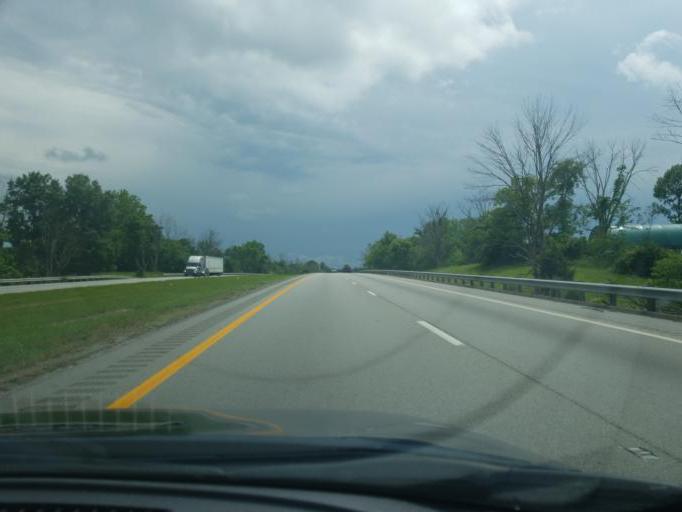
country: US
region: Kentucky
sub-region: Trimble County
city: Providence
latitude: 38.5767
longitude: -85.1815
